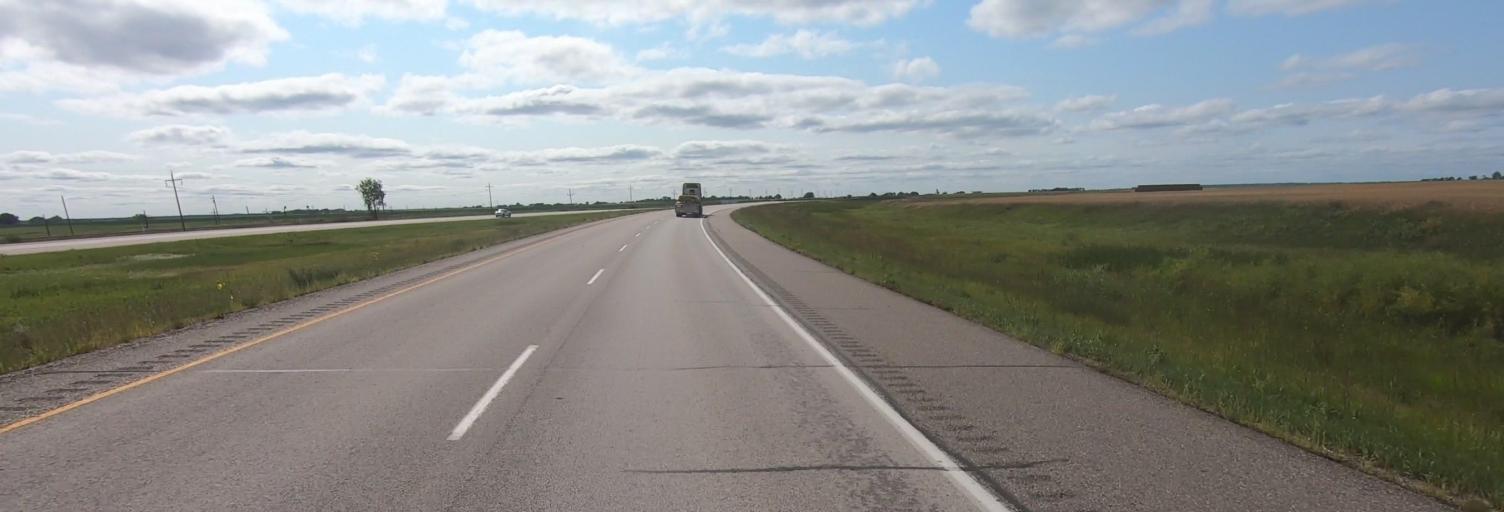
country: CA
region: Manitoba
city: Souris
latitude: 49.7847
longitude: -100.4300
